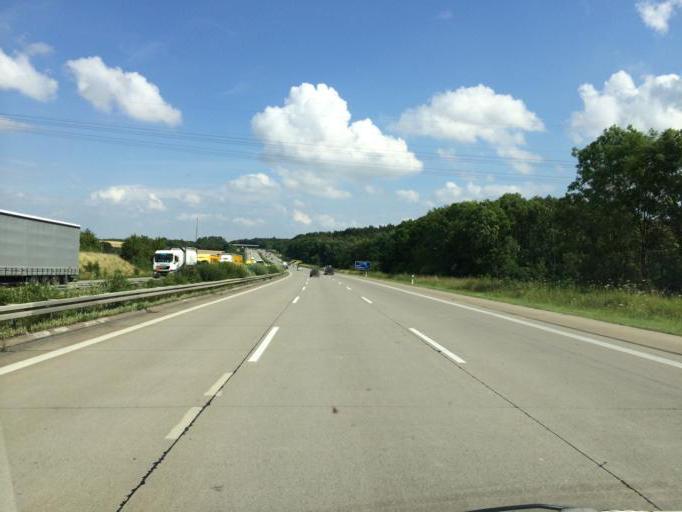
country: DE
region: Saxony-Anhalt
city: Beendorf
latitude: 52.2134
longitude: 11.0958
